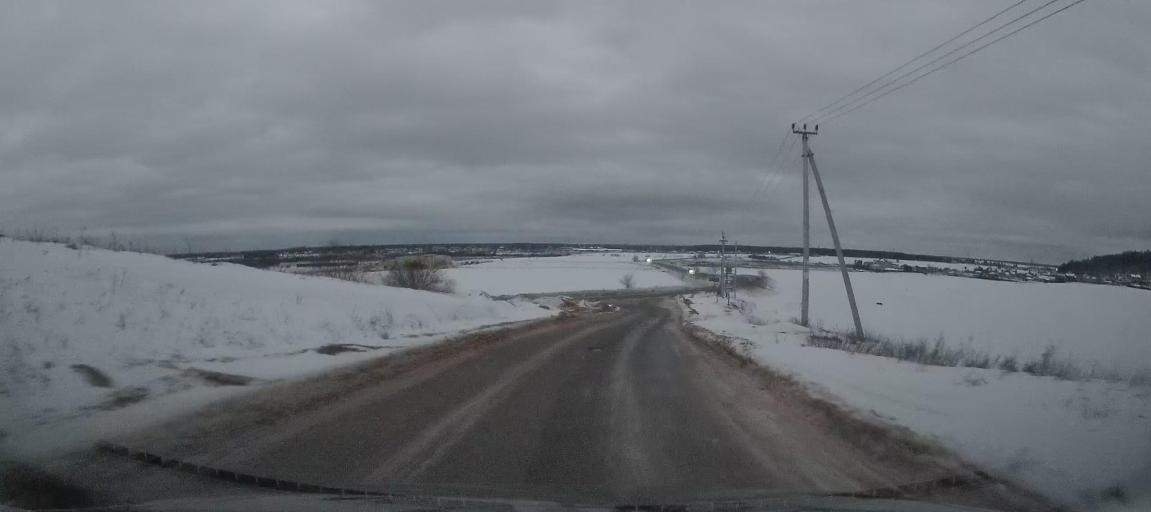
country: RU
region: Leningrad
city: Taytsy
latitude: 59.6928
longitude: 30.1448
